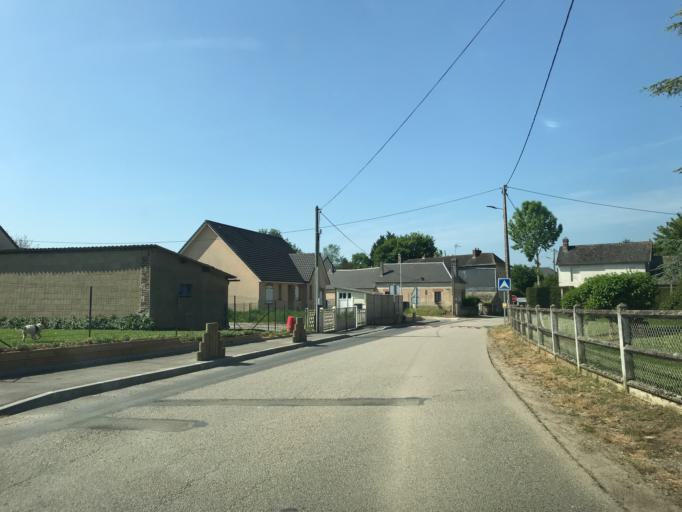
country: FR
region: Haute-Normandie
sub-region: Departement de la Seine-Maritime
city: Les Authieux-sur-le-Port-Saint-Ouen
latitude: 49.3553
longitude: 1.1520
